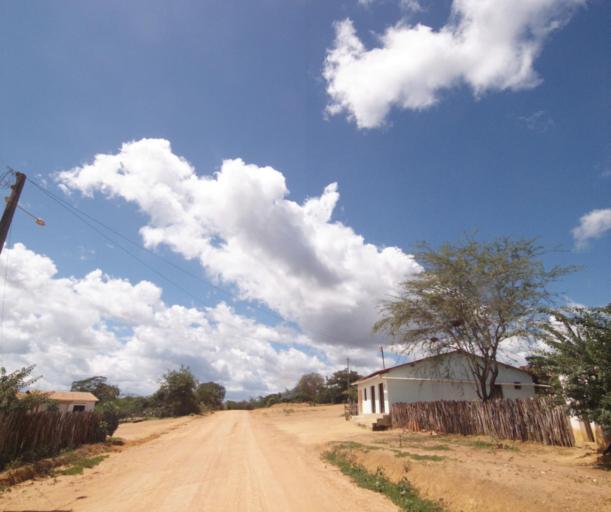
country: BR
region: Bahia
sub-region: Pocoes
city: Pocoes
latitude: -14.3319
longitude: -40.5969
